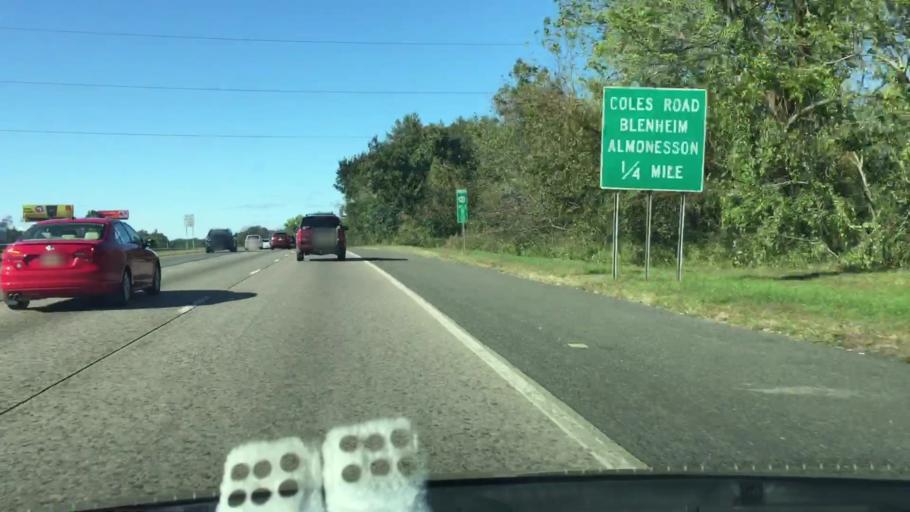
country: US
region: New Jersey
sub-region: Camden County
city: Blackwood
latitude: 39.8074
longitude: -75.0582
